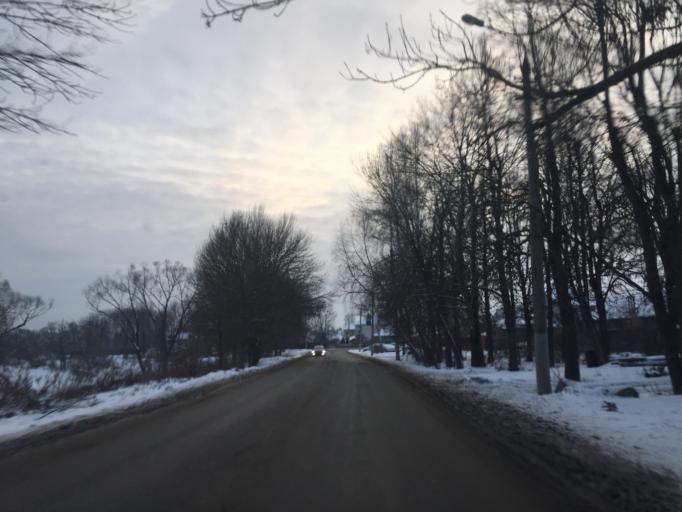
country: RU
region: Tula
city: Gorelki
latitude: 54.2343
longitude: 37.6413
